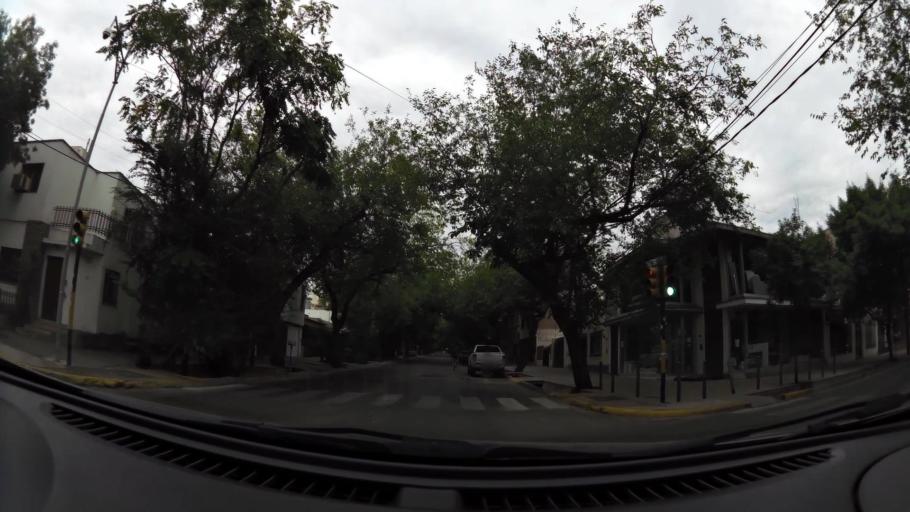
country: AR
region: Mendoza
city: Mendoza
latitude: -32.8994
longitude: -68.8450
